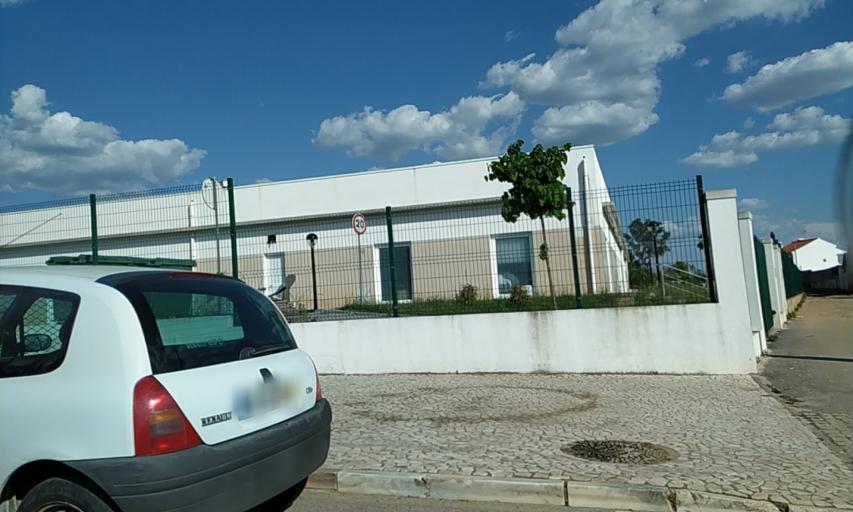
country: PT
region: Evora
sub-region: Estremoz
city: Estremoz
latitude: 38.8530
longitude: -7.5830
